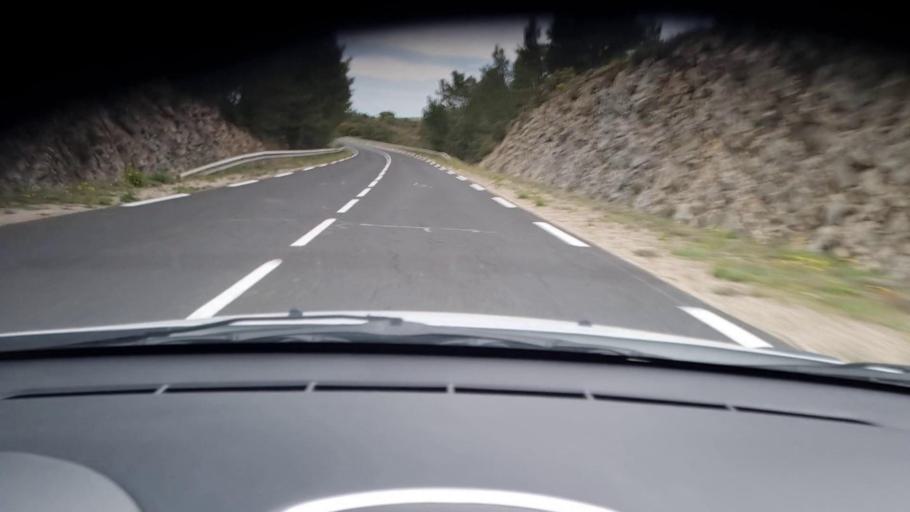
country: FR
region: Languedoc-Roussillon
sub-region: Departement du Gard
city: Poulx
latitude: 43.8937
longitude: 4.3878
